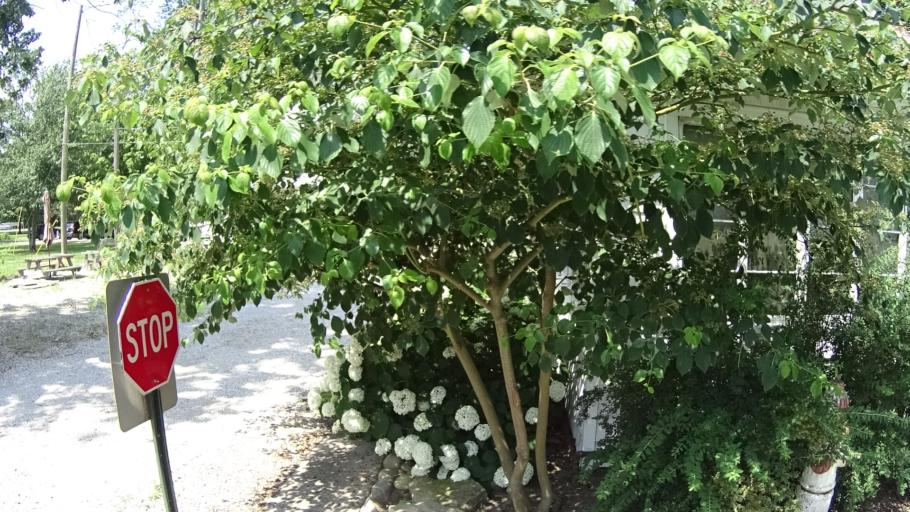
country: US
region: Ohio
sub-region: Lorain County
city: Vermilion
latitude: 41.4252
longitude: -82.3538
